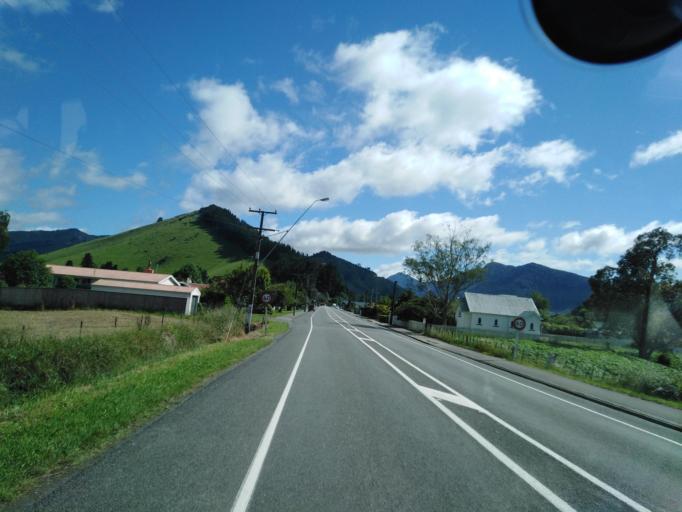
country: NZ
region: Nelson
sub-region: Nelson City
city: Nelson
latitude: -41.2312
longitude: 173.5820
